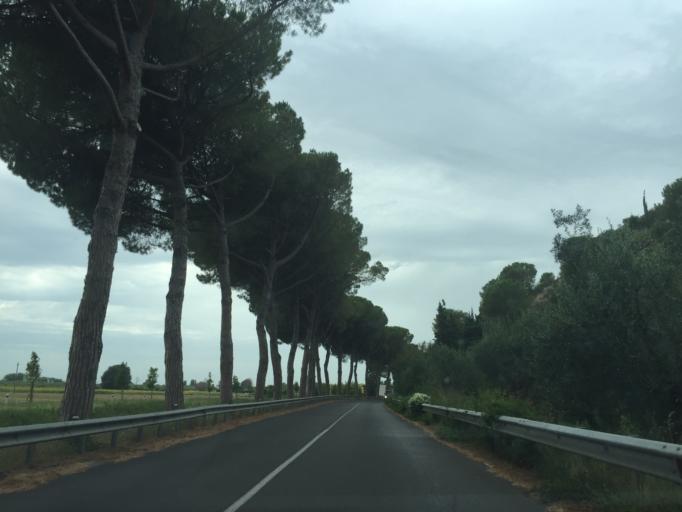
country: IT
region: Tuscany
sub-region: Province of Pisa
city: Uliveto Terme
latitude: 43.7023
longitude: 10.5112
